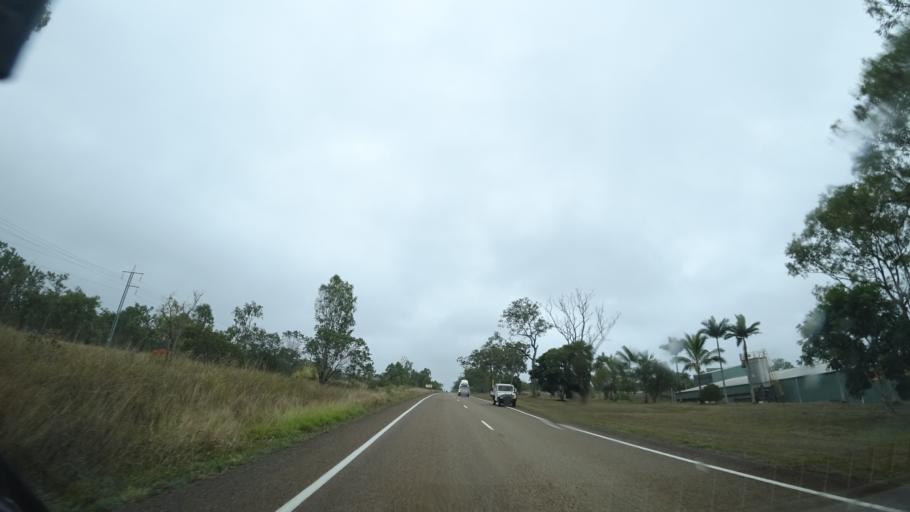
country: AU
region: Queensland
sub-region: Tablelands
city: Ravenshoe
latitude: -17.6984
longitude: 145.1947
